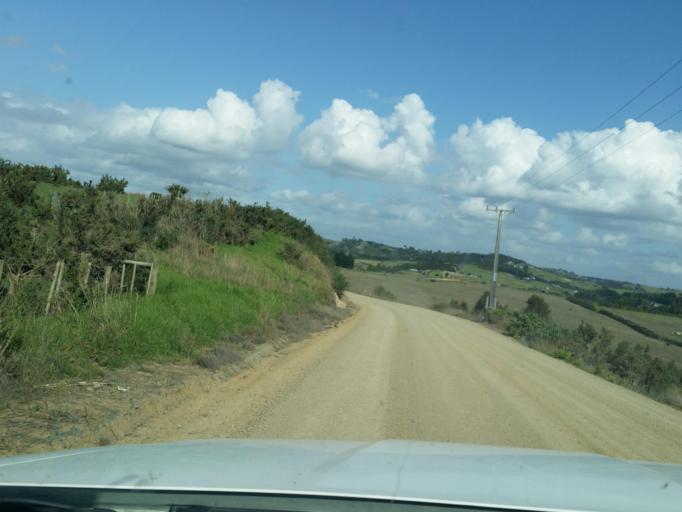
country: NZ
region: Auckland
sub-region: Auckland
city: Wellsford
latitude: -36.1449
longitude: 174.5408
